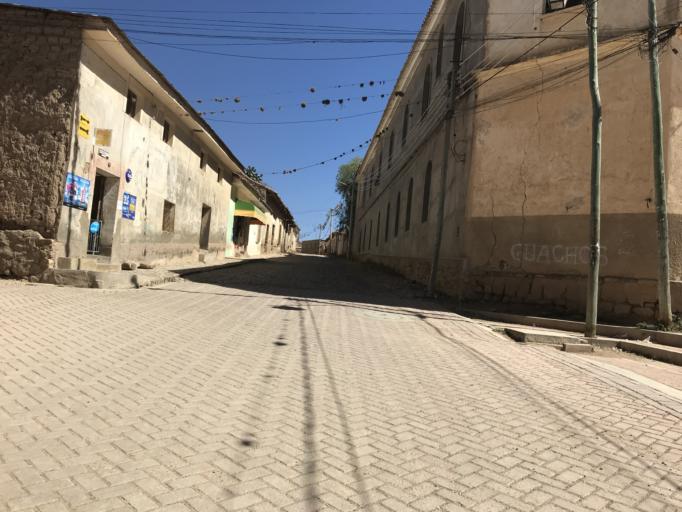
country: BO
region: Cochabamba
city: Tarata
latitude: -17.6157
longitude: -66.0294
